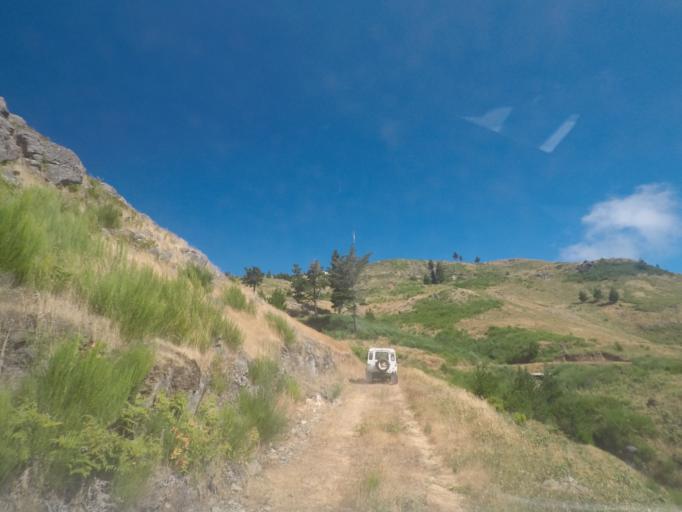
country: PT
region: Madeira
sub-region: Funchal
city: Nossa Senhora do Monte
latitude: 32.7070
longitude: -16.9065
